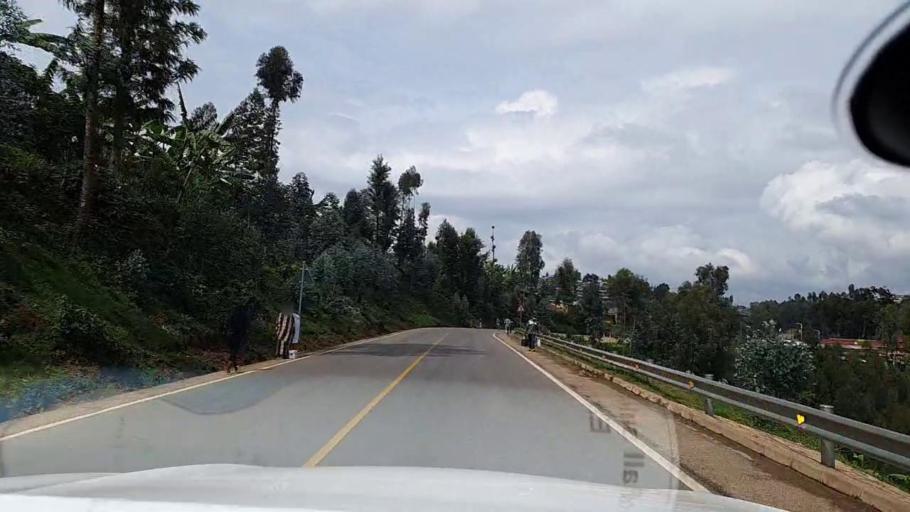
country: RW
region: Southern Province
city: Nzega
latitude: -2.4849
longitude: 29.5307
